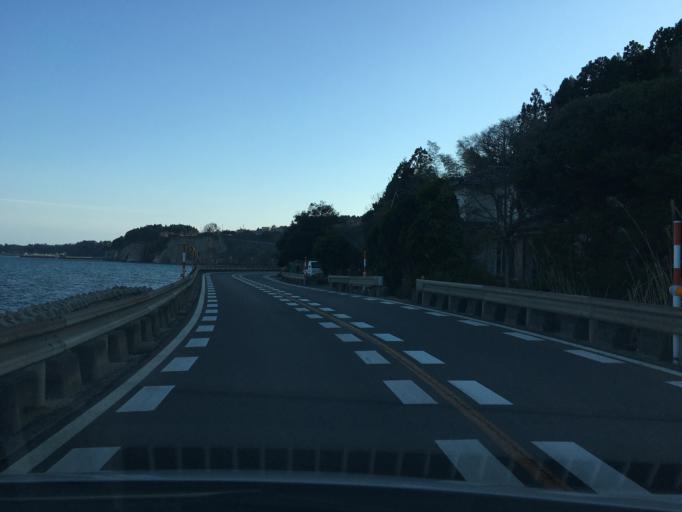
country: JP
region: Ishikawa
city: Nanao
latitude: 36.9898
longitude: 137.0513
